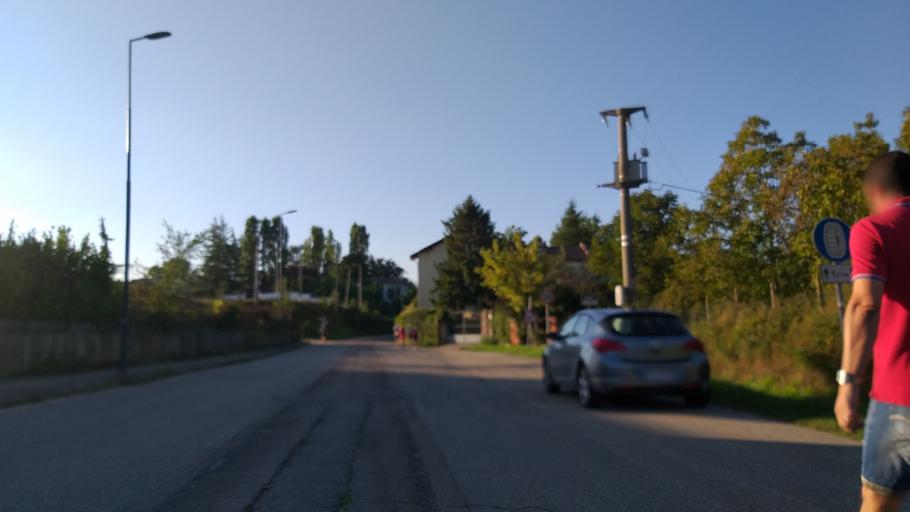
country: IT
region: Piedmont
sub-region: Provincia di Asti
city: Asti
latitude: 44.9194
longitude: 8.2005
